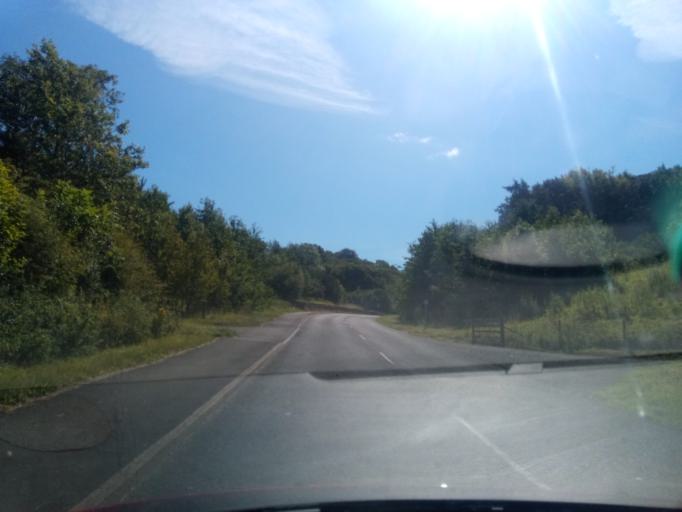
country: GB
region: England
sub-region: Northumberland
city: Bardon Mill
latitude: 54.9686
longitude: -2.2443
